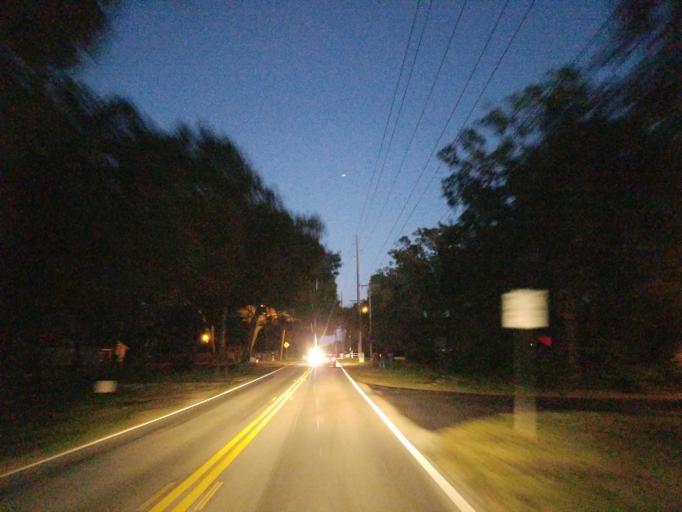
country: US
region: Florida
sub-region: Hillsborough County
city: Bloomingdale
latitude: 27.8939
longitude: -82.2185
